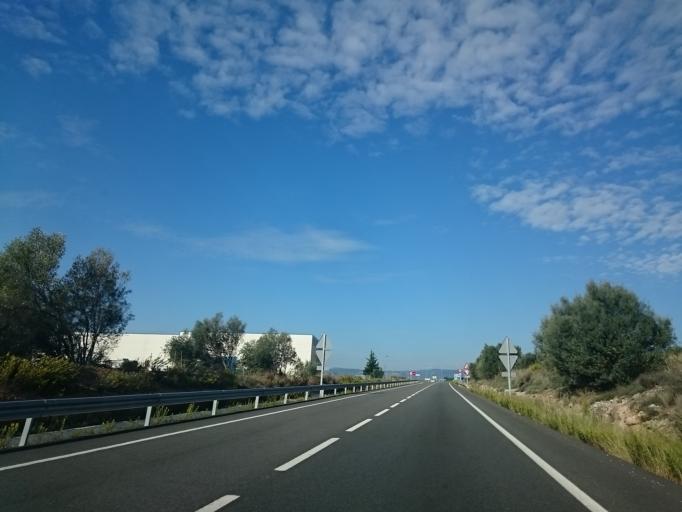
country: ES
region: Catalonia
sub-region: Provincia de Tarragona
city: Montferri
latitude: 41.2914
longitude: 1.3464
